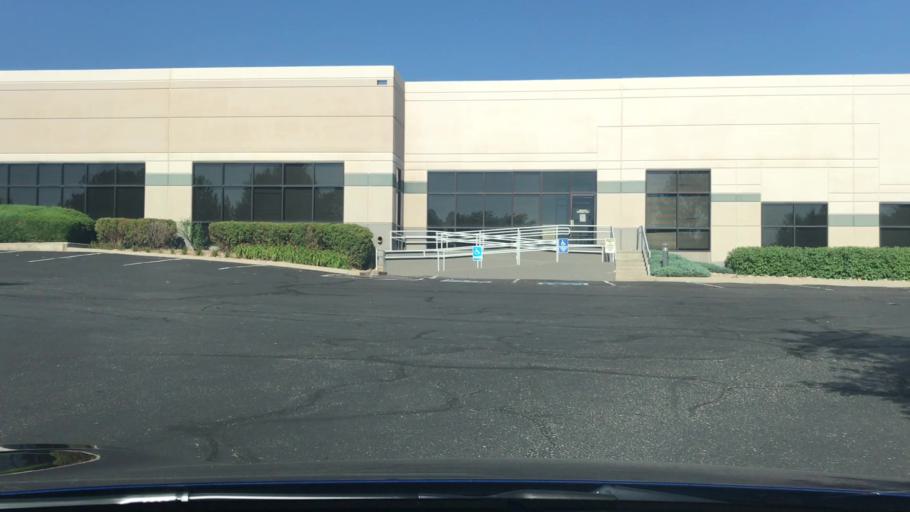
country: US
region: Colorado
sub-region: Arapahoe County
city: Dove Valley
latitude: 39.5940
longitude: -104.8408
